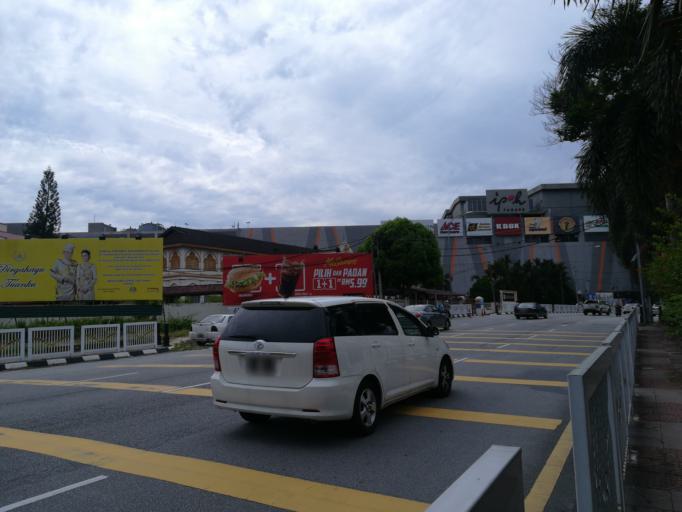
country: MY
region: Perak
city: Ipoh
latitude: 4.5959
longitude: 101.0884
